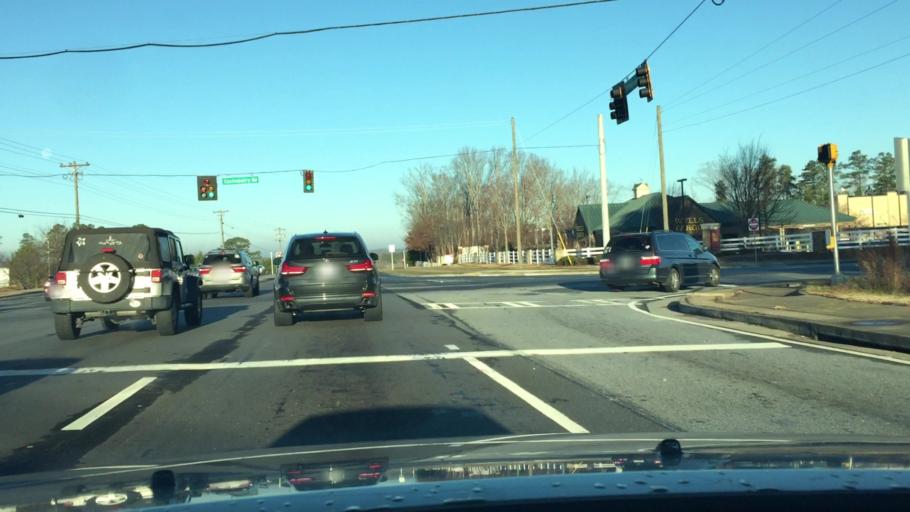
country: US
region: Georgia
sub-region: Forsyth County
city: Cumming
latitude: 34.1726
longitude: -84.1864
